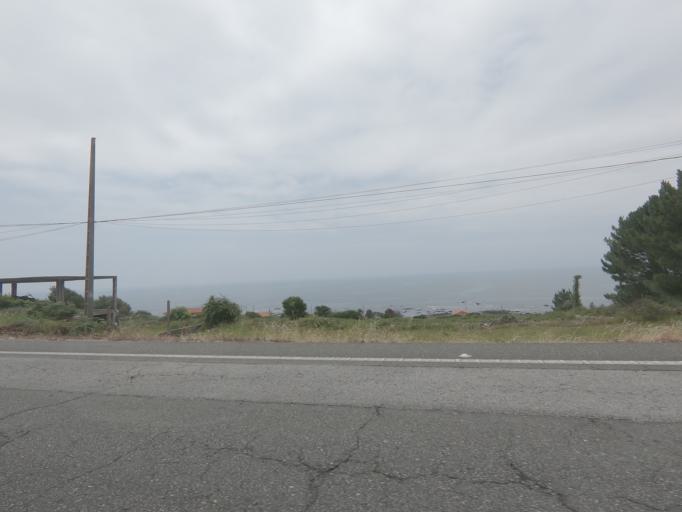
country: ES
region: Galicia
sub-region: Provincia de Pontevedra
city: Oia
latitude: 41.9950
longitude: -8.8787
